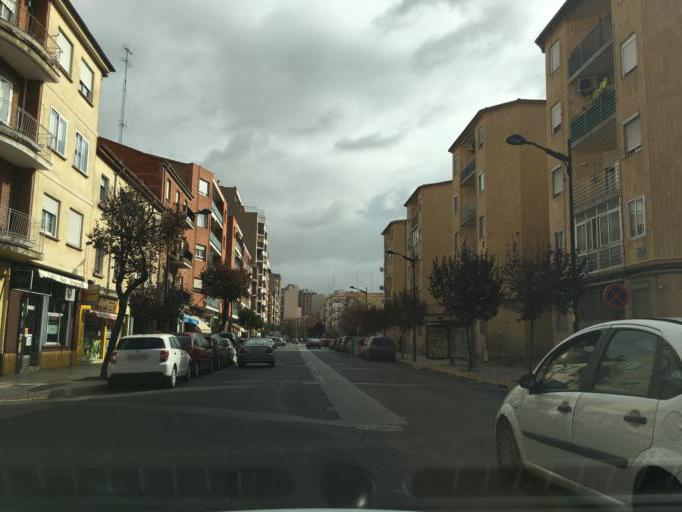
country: ES
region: Castille-La Mancha
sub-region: Provincia de Albacete
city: Albacete
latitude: 38.9889
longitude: -1.8645
